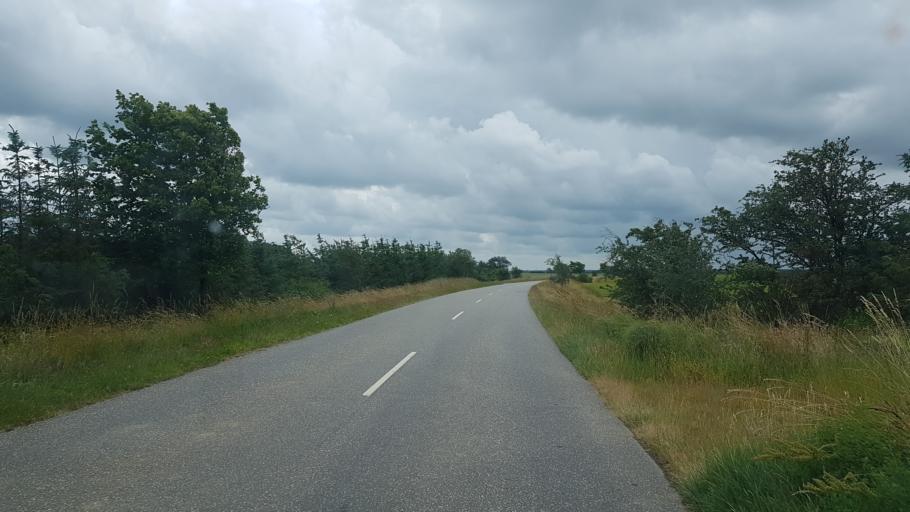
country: DK
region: South Denmark
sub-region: Kolding Kommune
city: Vamdrup
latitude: 55.4456
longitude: 9.2719
